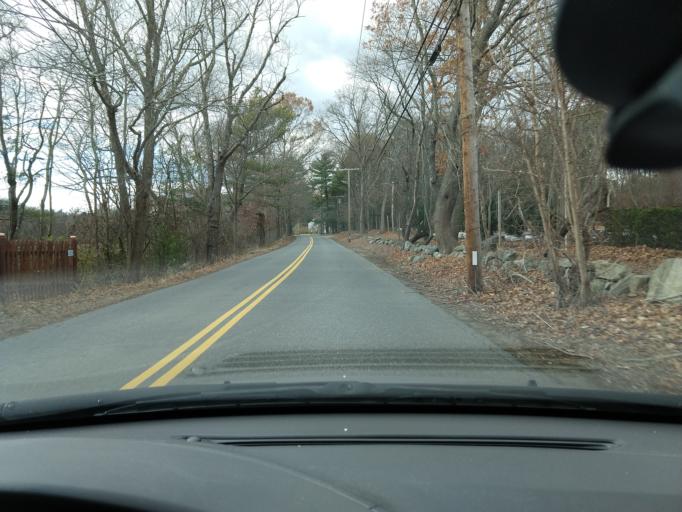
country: US
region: Massachusetts
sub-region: Middlesex County
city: Sudbury
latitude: 42.3969
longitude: -71.3881
